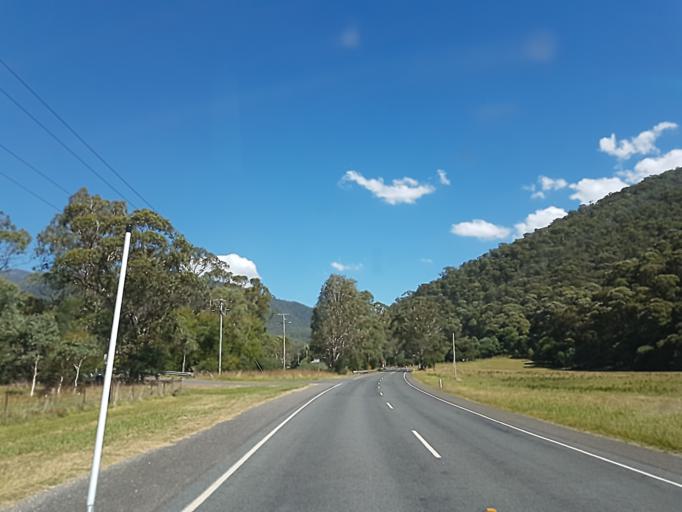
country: AU
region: Victoria
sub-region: Alpine
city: Mount Beauty
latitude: -36.8422
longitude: 147.0785
